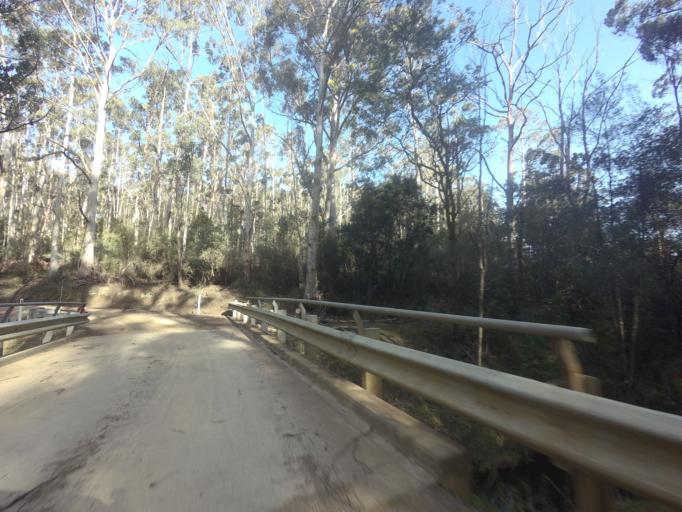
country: AU
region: Tasmania
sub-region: Kingborough
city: Kettering
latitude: -43.1070
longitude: 147.2562
